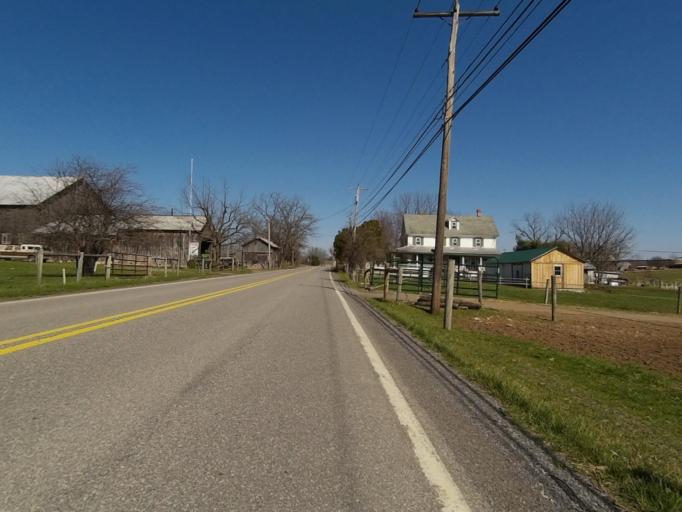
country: US
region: Pennsylvania
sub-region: Centre County
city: Stormstown
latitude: 40.7813
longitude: -78.0368
